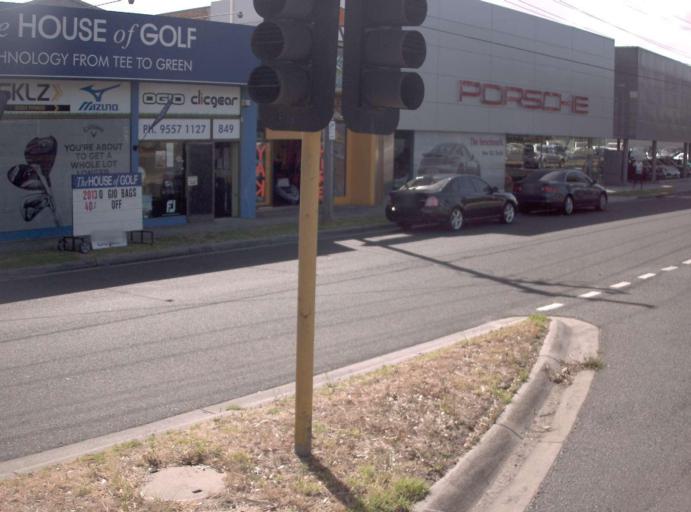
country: AU
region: Victoria
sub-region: Glen Eira
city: Bentleigh
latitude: -37.9255
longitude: 145.0273
